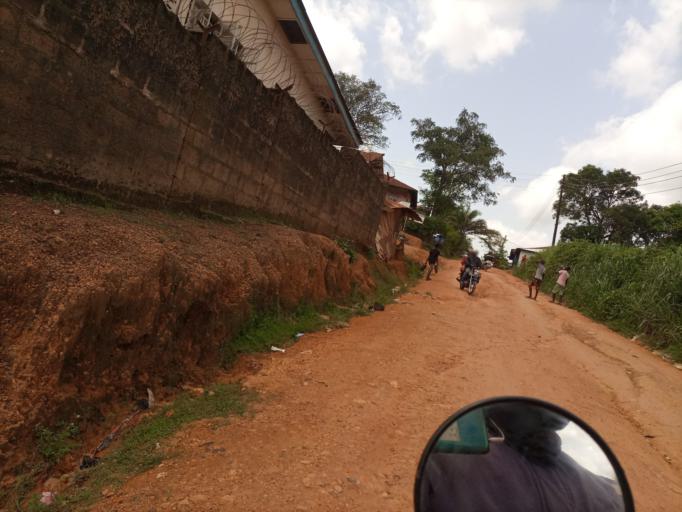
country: SL
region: Southern Province
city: Bo
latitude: 7.9514
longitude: -11.7355
